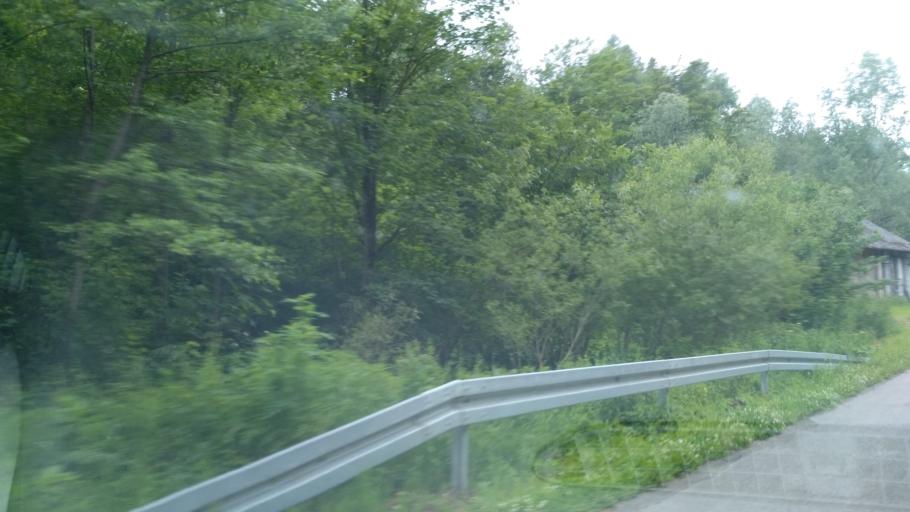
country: PL
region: Subcarpathian Voivodeship
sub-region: Powiat przemyski
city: Nienadowa
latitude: 49.8771
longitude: 22.4130
